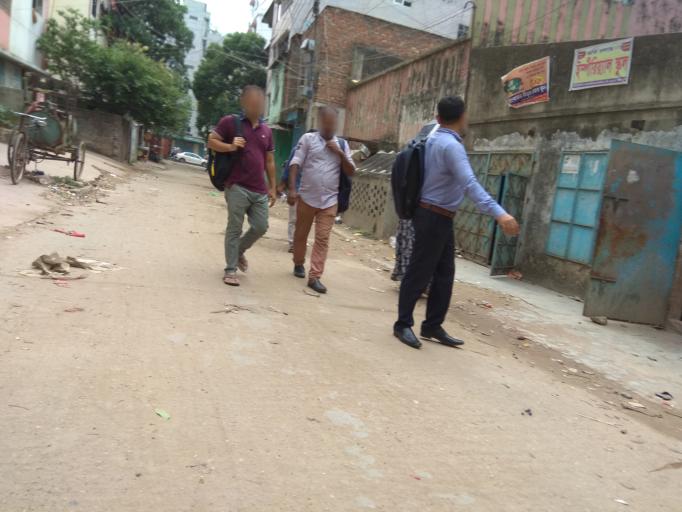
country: BD
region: Dhaka
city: Tungi
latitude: 23.8169
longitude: 90.3718
